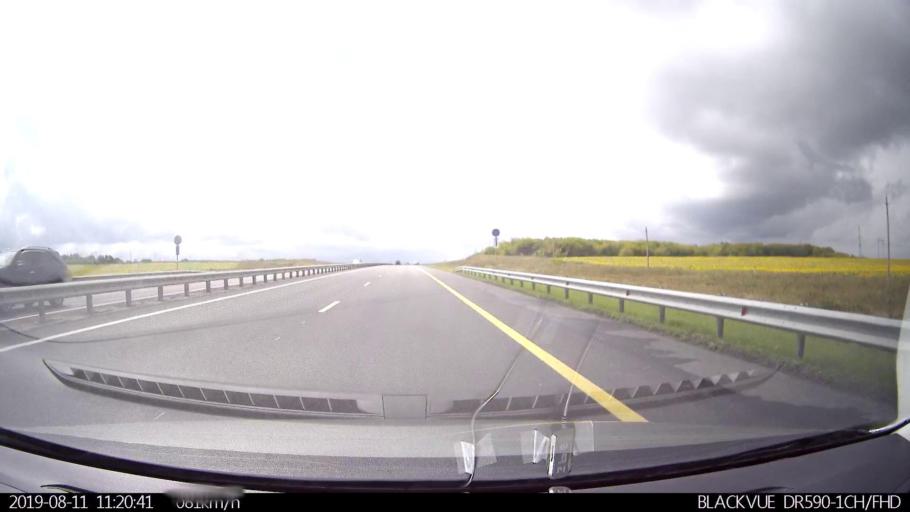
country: RU
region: Ulyanovsk
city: Novoul'yanovsk
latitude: 54.1548
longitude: 48.2642
